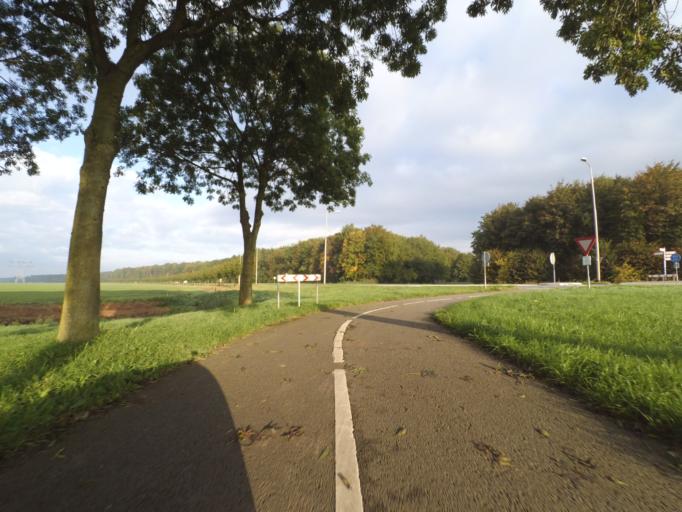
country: NL
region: Flevoland
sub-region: Gemeente Dronten
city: Dronten
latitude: 52.5165
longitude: 5.6894
